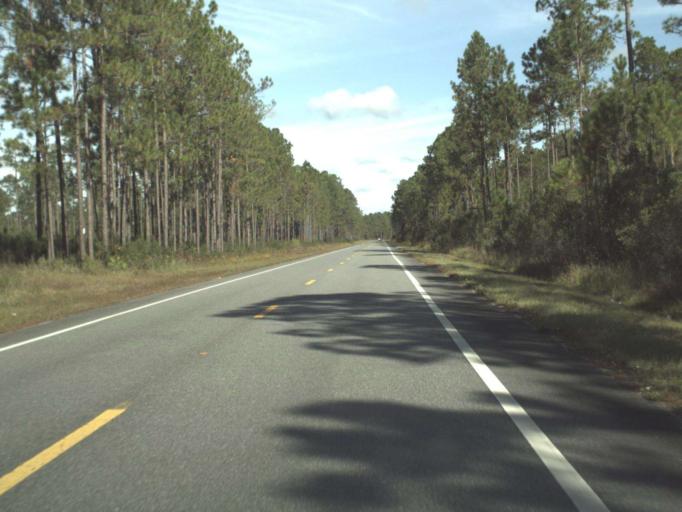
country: US
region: Florida
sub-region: Franklin County
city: Apalachicola
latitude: 29.8899
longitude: -84.9772
